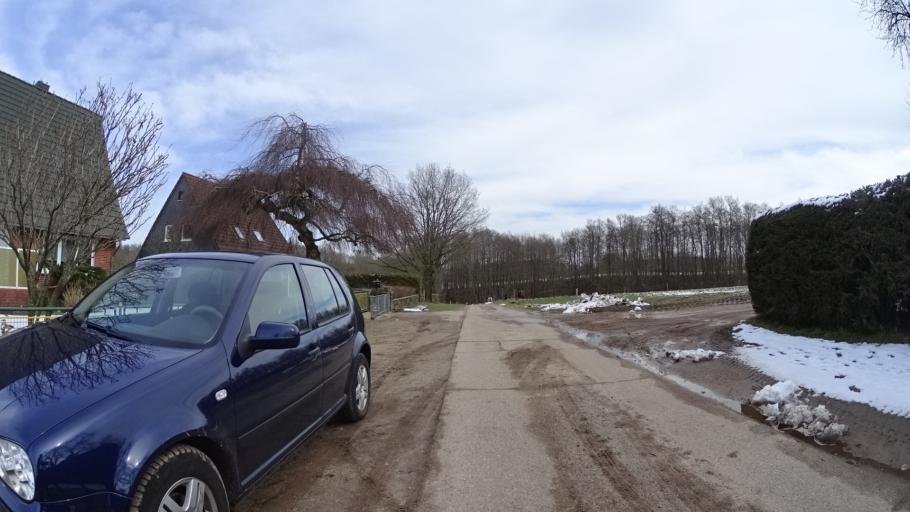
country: DE
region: Schleswig-Holstein
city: Kuhren
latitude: 54.1967
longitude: 10.2469
